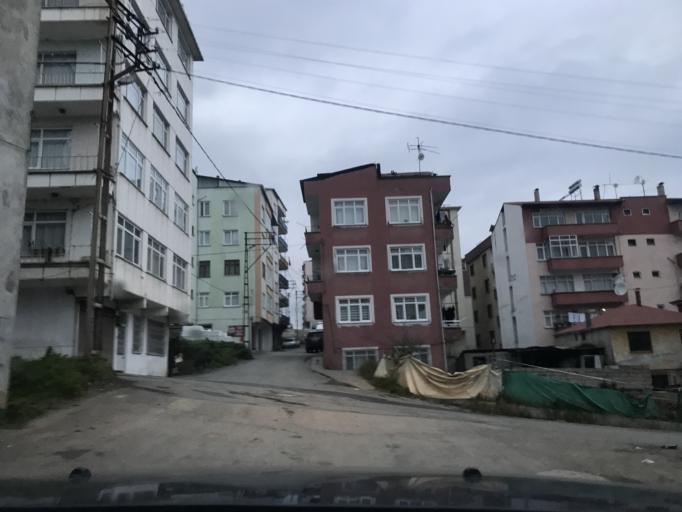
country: TR
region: Trabzon
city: Akcaabat
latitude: 41.0152
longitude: 39.5898
